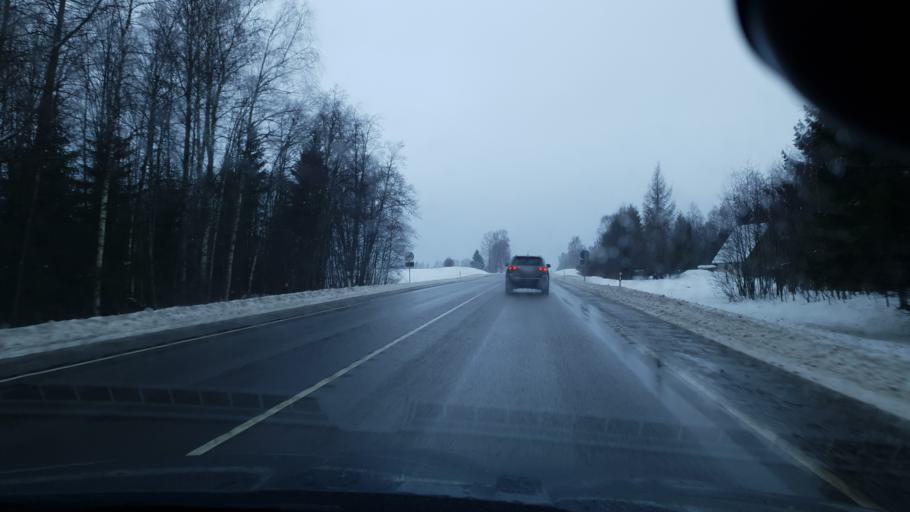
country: EE
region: Harju
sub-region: Anija vald
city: Kehra
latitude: 59.1076
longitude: 25.3237
